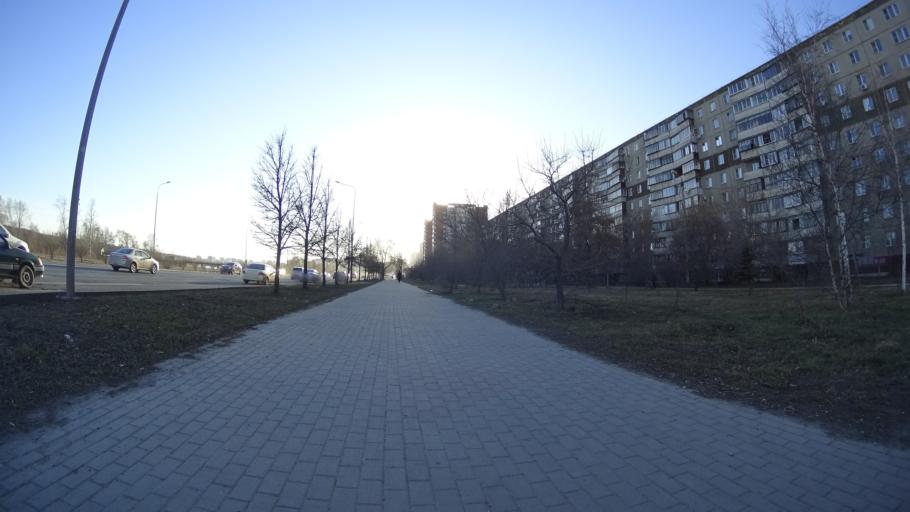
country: RU
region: Chelyabinsk
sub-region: Gorod Chelyabinsk
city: Chelyabinsk
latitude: 55.1748
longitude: 61.3456
